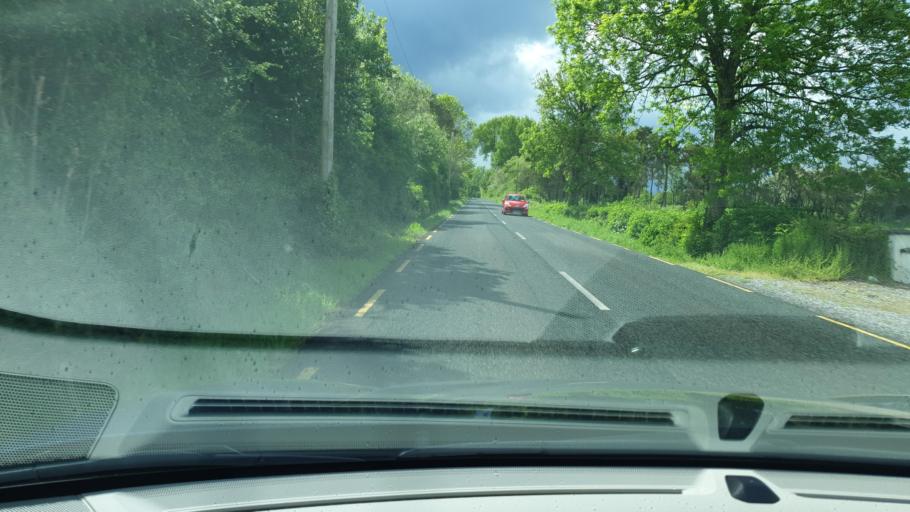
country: IE
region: Leinster
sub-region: Uibh Fhaili
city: Clara
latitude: 53.2366
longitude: -7.6631
